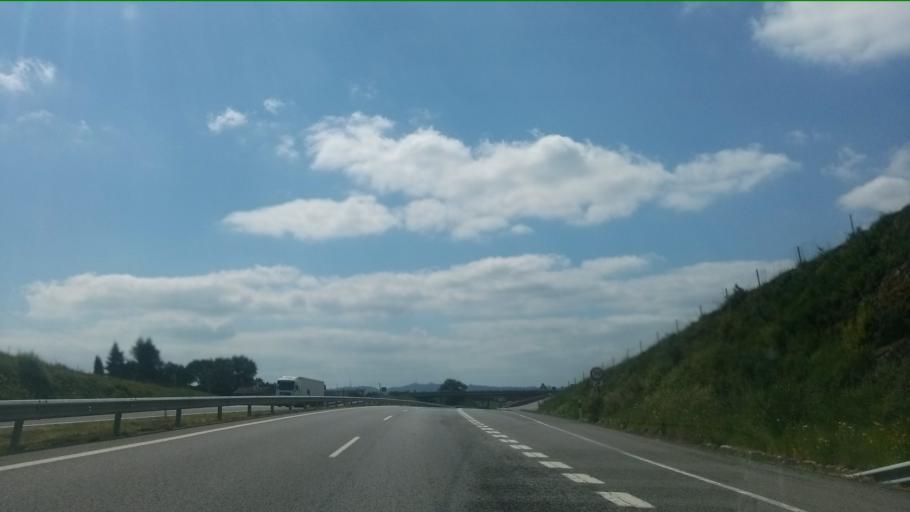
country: ES
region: Galicia
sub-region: Provincia da Coruna
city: Santiago de Compostela
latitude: 42.8962
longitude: -8.4788
